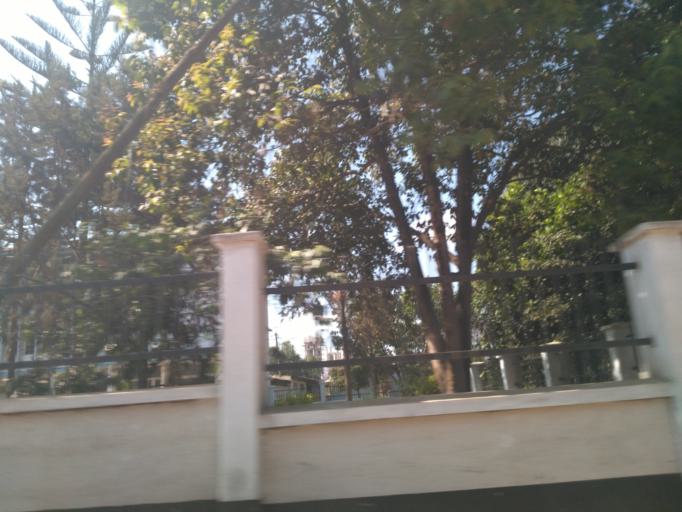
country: TZ
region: Arusha
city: Arusha
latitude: -3.3693
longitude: 36.6917
